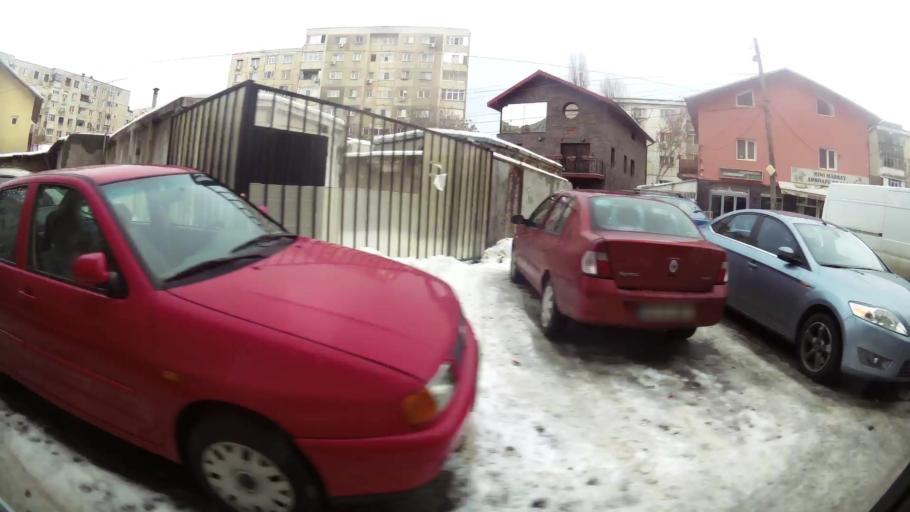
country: RO
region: Bucuresti
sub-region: Municipiul Bucuresti
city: Bucuresti
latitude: 44.4075
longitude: 26.0640
